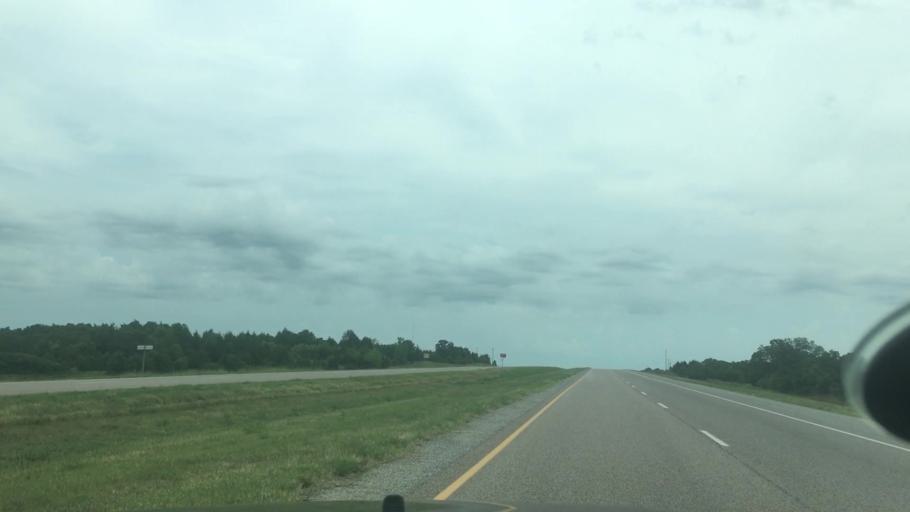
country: US
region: Oklahoma
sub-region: Pontotoc County
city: Byng
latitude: 34.8689
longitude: -96.6793
